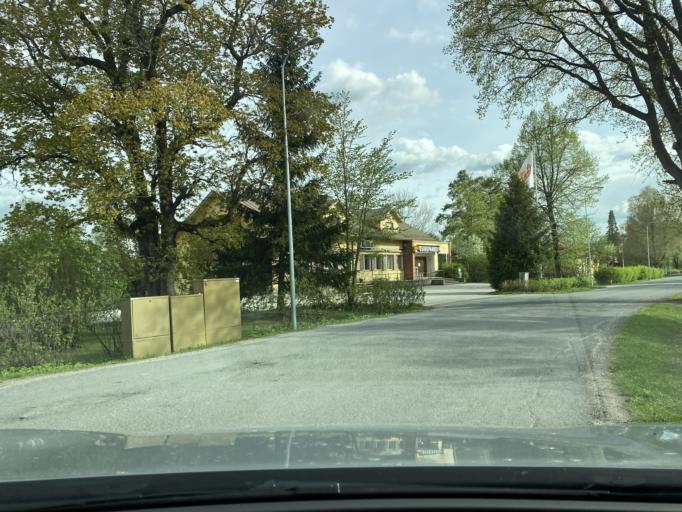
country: FI
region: Varsinais-Suomi
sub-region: Salo
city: Kiikala
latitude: 60.4613
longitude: 23.5519
